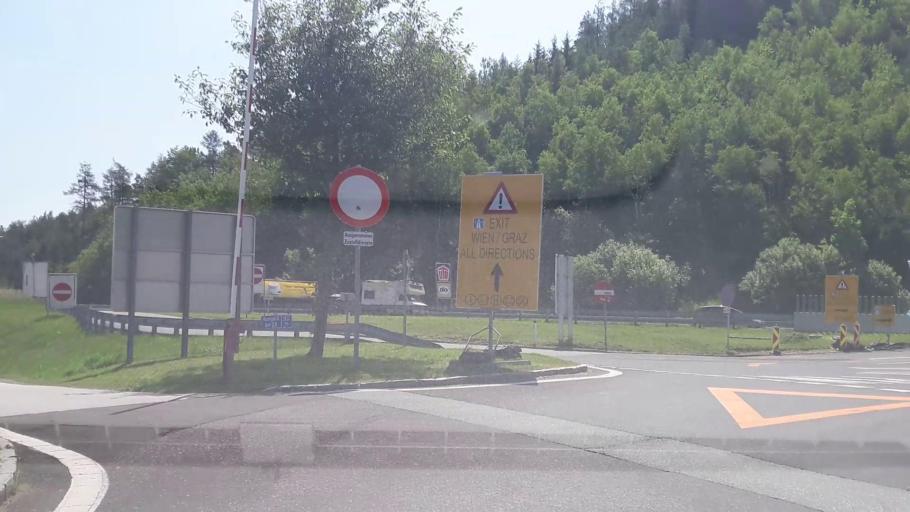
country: AT
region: Lower Austria
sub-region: Politischer Bezirk Neunkirchen
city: Thomasberg
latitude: 47.5434
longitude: 16.1172
